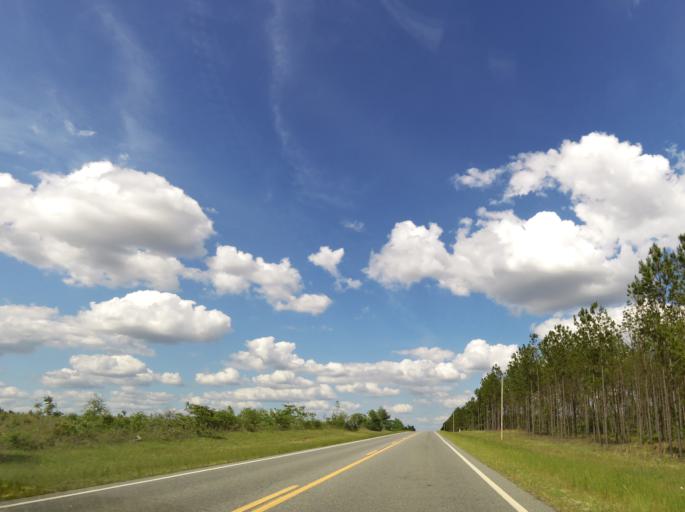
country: US
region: Georgia
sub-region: Treutlen County
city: Soperton
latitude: 32.2801
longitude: -82.7063
